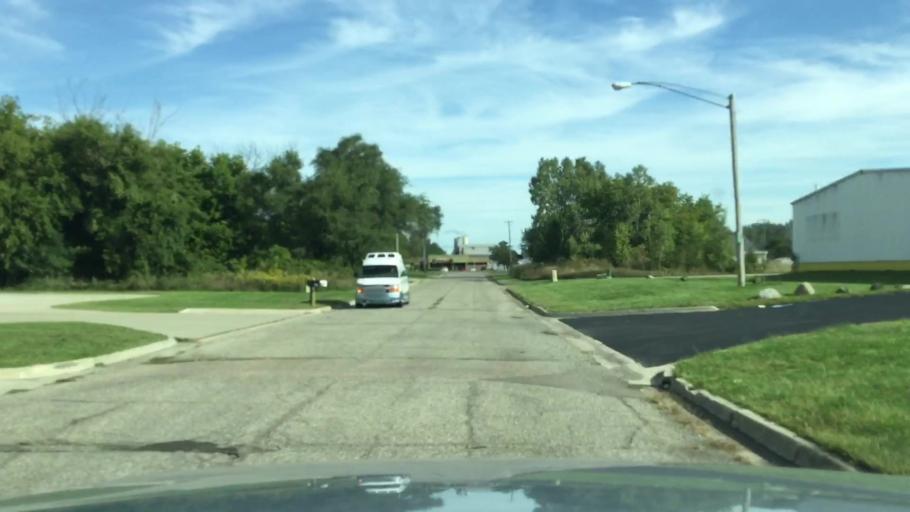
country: US
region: Michigan
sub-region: Genesee County
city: Flushing
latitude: 43.0582
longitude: -83.8099
